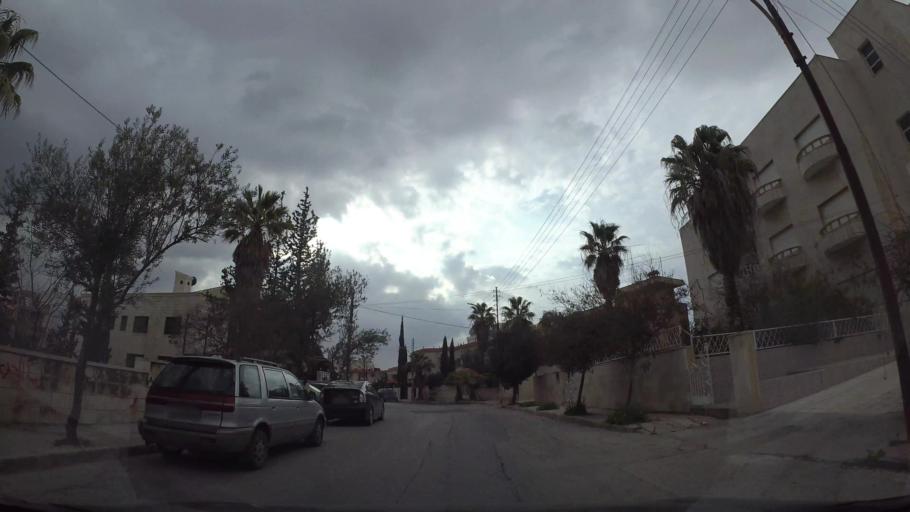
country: JO
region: Amman
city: Amman
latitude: 32.0049
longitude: 35.9439
